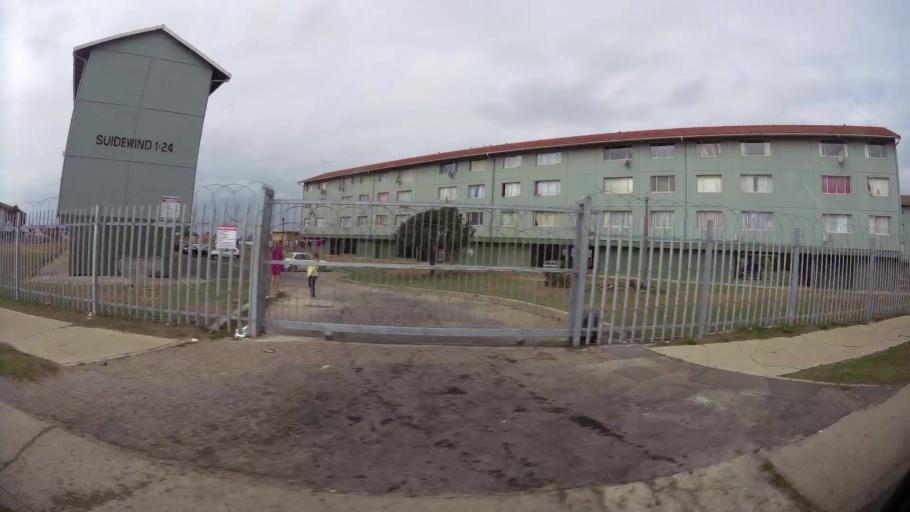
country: ZA
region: Eastern Cape
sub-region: Nelson Mandela Bay Metropolitan Municipality
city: Port Elizabeth
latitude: -33.8948
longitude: 25.5532
